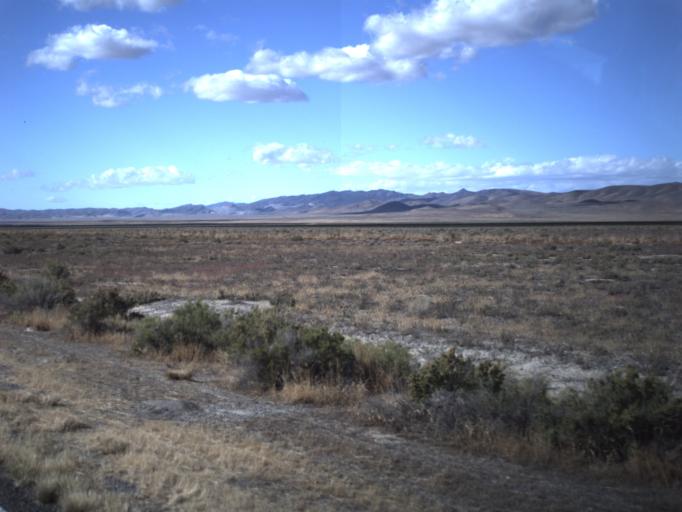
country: US
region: Utah
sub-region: Millard County
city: Delta
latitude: 39.0747
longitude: -112.7578
